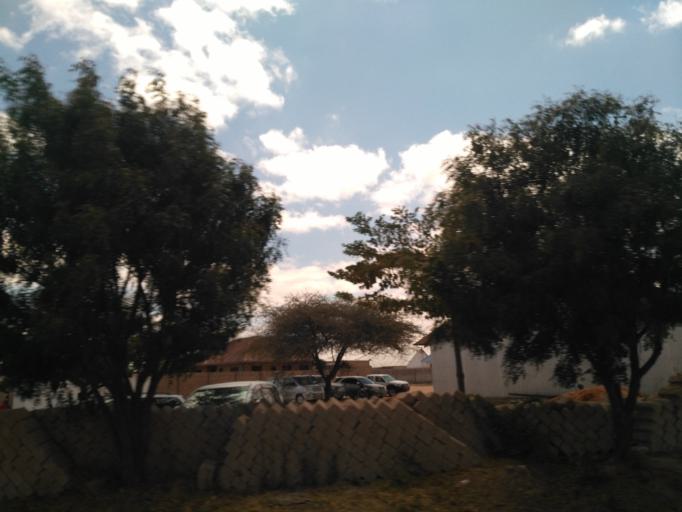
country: TZ
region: Dodoma
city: Kisasa
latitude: -6.1805
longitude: 35.7950
